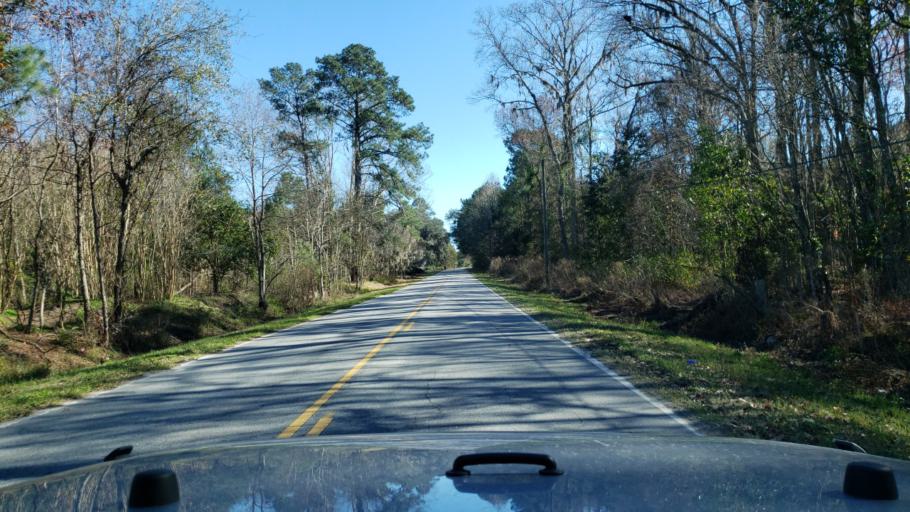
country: US
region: Georgia
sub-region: Chatham County
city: Georgetown
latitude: 32.0329
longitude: -81.1870
